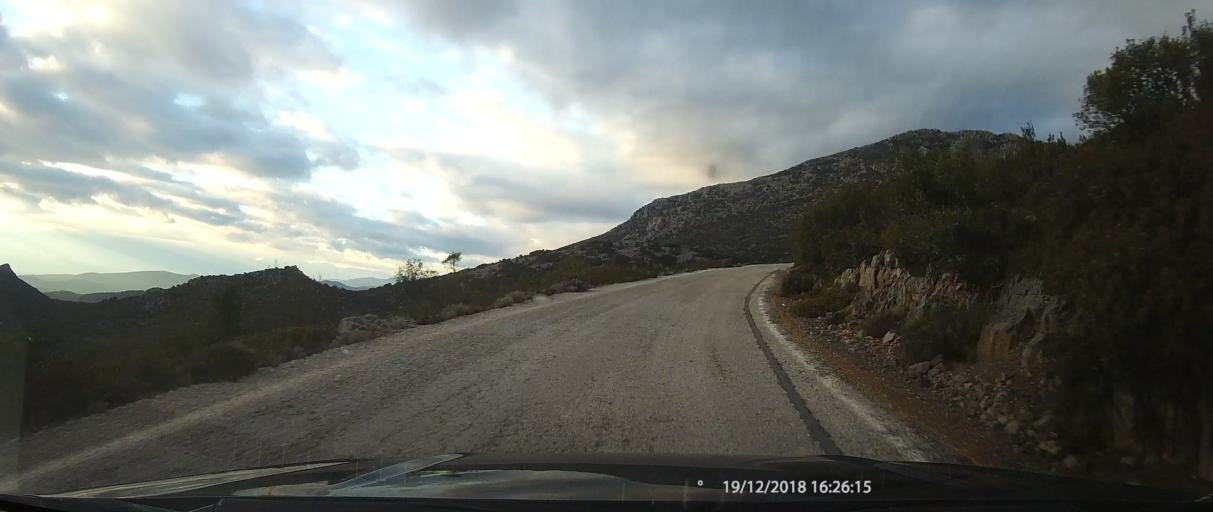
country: GR
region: Peloponnese
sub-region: Nomos Lakonias
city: Kato Glikovrisi
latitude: 36.9588
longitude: 22.8513
